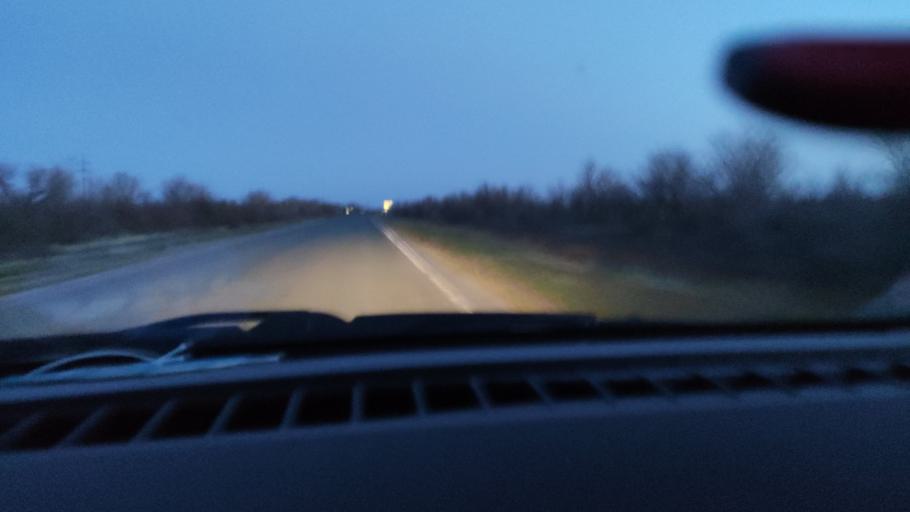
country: RU
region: Saratov
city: Rovnoye
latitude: 50.9449
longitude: 46.1262
